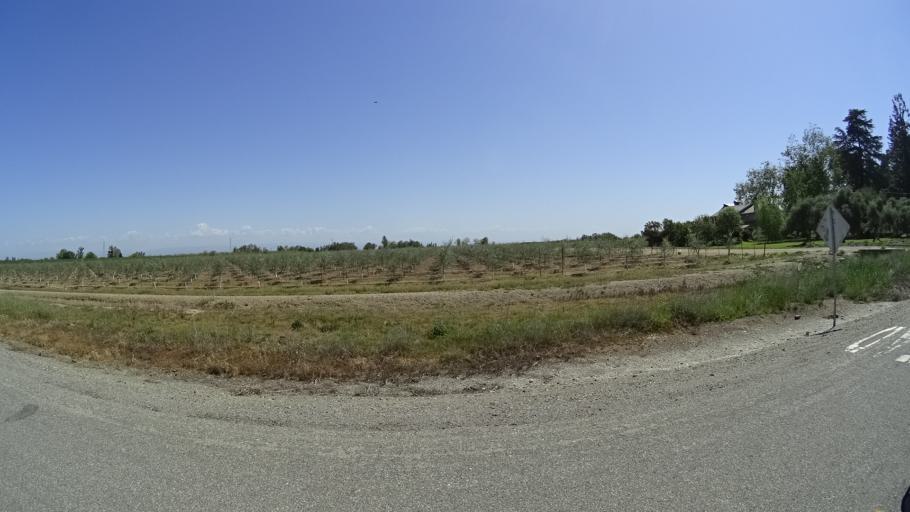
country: US
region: California
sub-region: Glenn County
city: Orland
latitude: 39.7851
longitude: -122.1691
